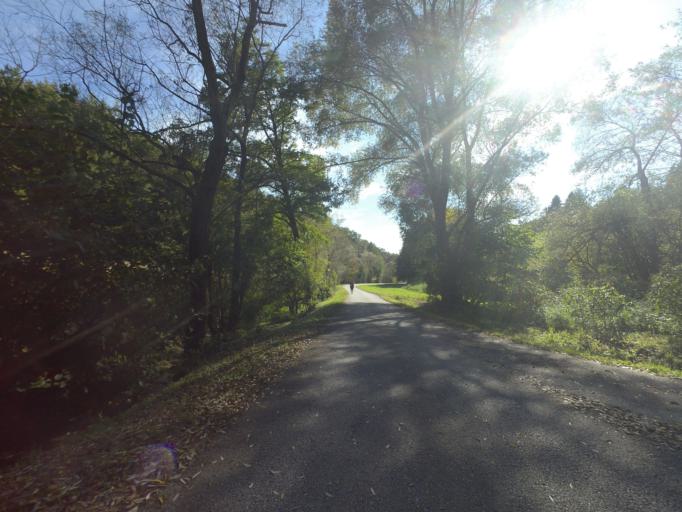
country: AT
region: Styria
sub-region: Politischer Bezirk Leibnitz
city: Kitzeck im Sausal
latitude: 46.7769
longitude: 15.4422
